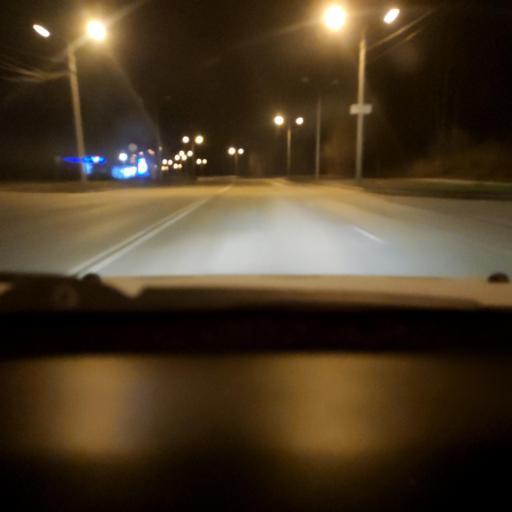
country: RU
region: Perm
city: Perm
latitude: 58.0651
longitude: 56.3647
